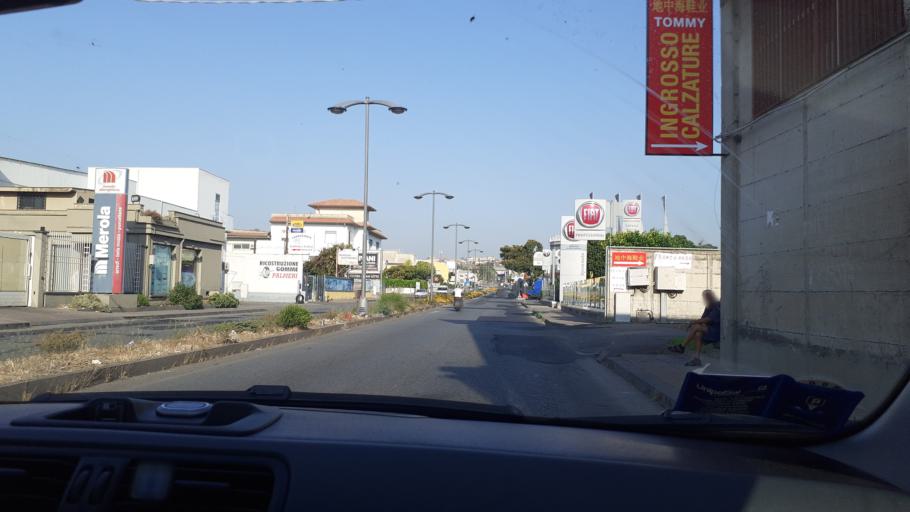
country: IT
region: Sicily
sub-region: Catania
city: Misterbianco
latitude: 37.5134
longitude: 15.0279
